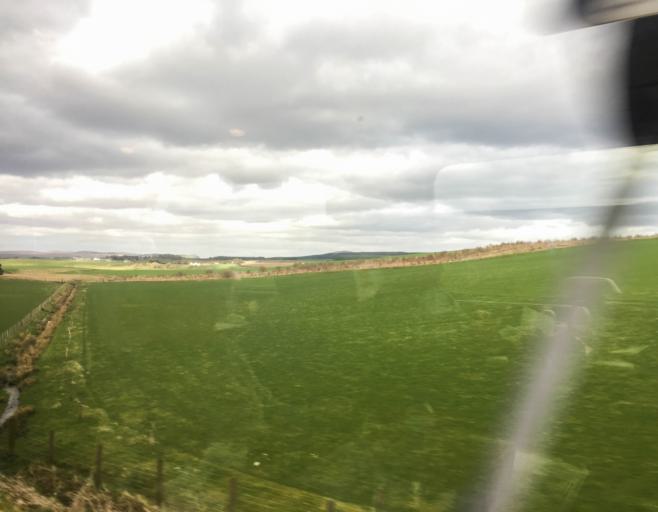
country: GB
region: Scotland
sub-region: South Lanarkshire
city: Carnwath
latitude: 55.6546
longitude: -3.6329
